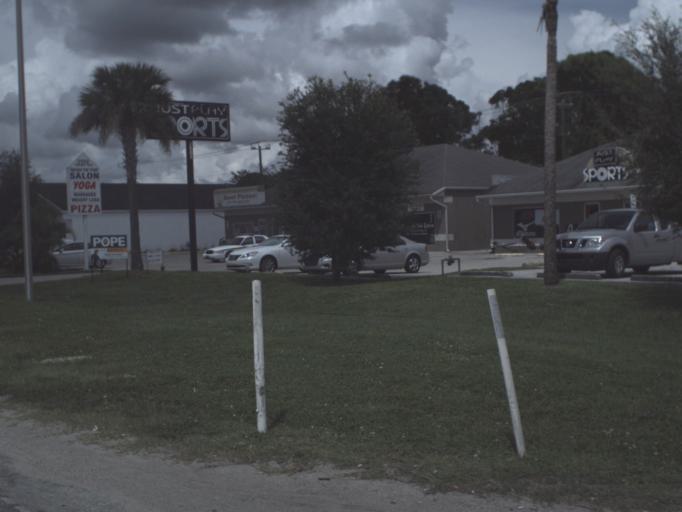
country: US
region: Florida
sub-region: Charlotte County
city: Port Charlotte
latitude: 26.9930
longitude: -82.1137
